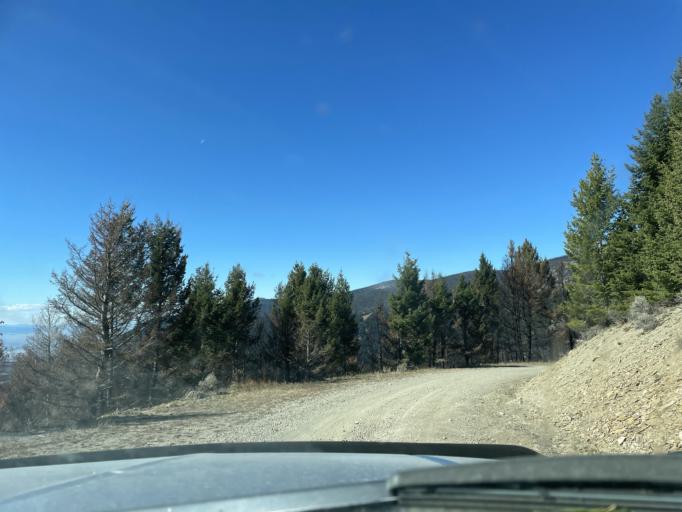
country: US
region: Montana
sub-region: Broadwater County
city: Townsend
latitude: 46.5018
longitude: -111.2754
